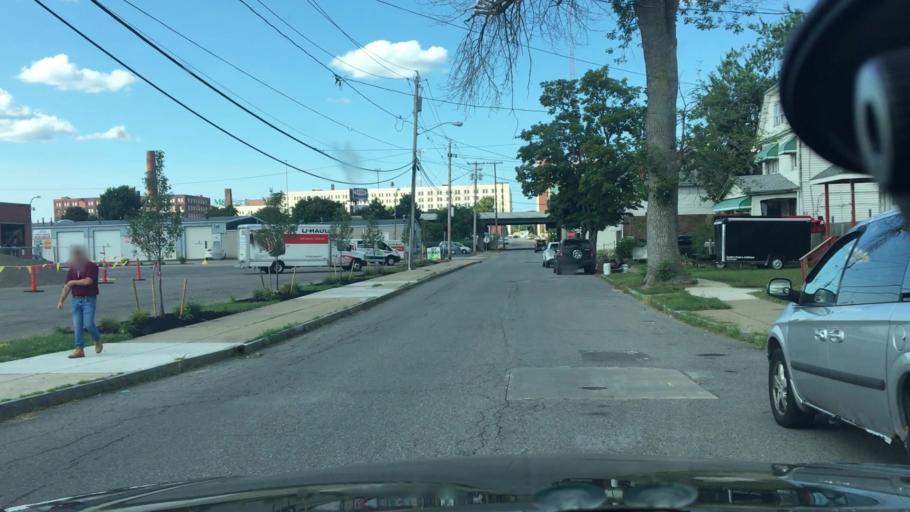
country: US
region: New York
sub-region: Erie County
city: Buffalo
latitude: 42.8707
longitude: -78.8520
